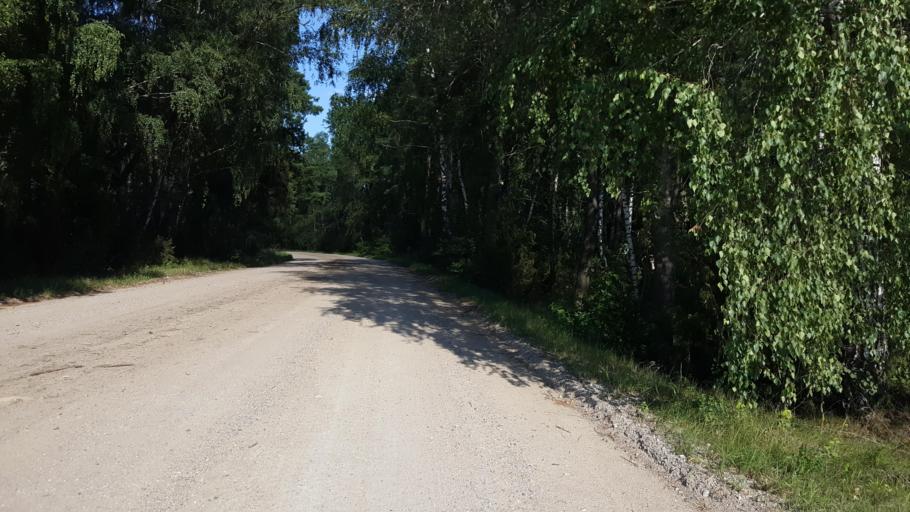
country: BY
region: Brest
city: Kamyanyets
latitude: 52.3637
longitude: 23.7205
